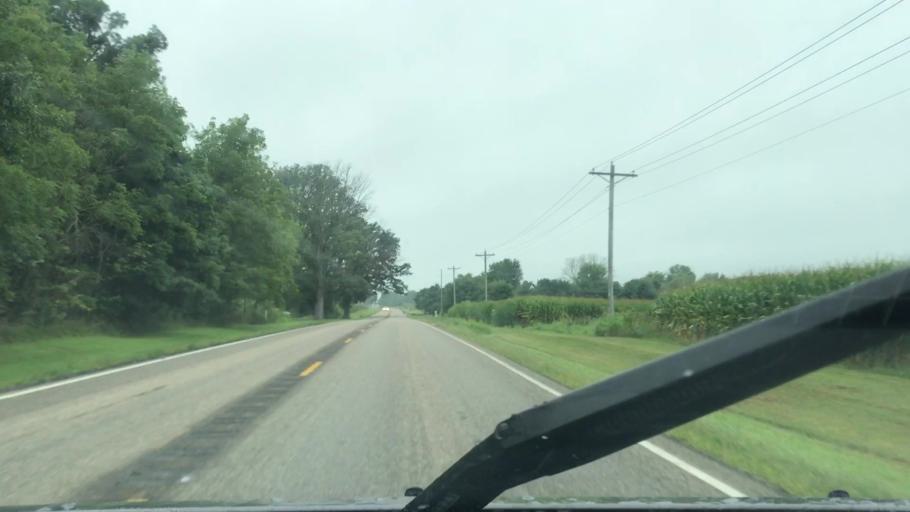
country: US
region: Indiana
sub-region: Hamilton County
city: Sheridan
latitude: 40.1278
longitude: -86.3407
